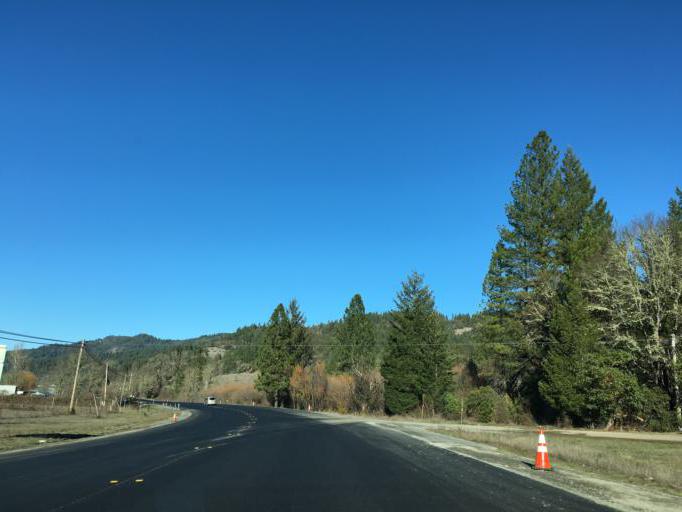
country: US
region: California
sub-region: Mendocino County
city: Laytonville
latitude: 39.6615
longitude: -123.4766
